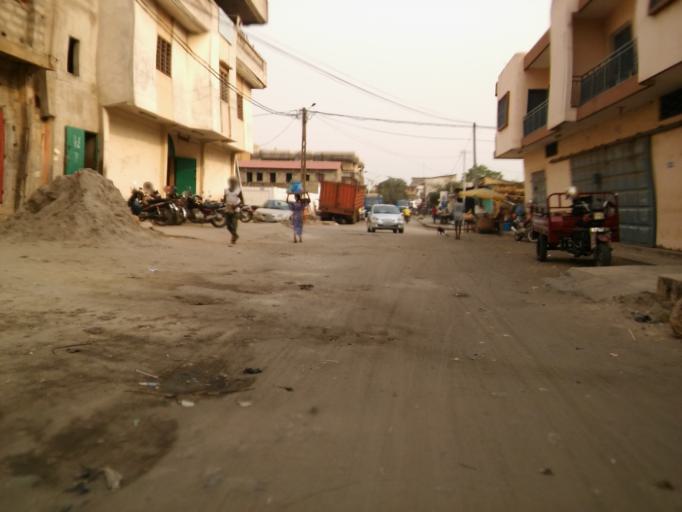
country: BJ
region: Littoral
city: Cotonou
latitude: 6.3740
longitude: 2.4102
